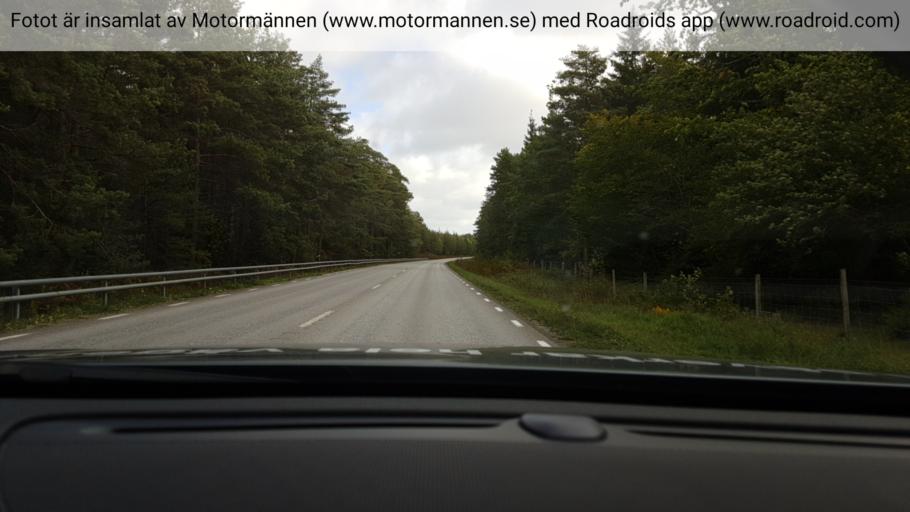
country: SE
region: Gotland
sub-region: Gotland
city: Slite
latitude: 57.8532
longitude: 18.9865
